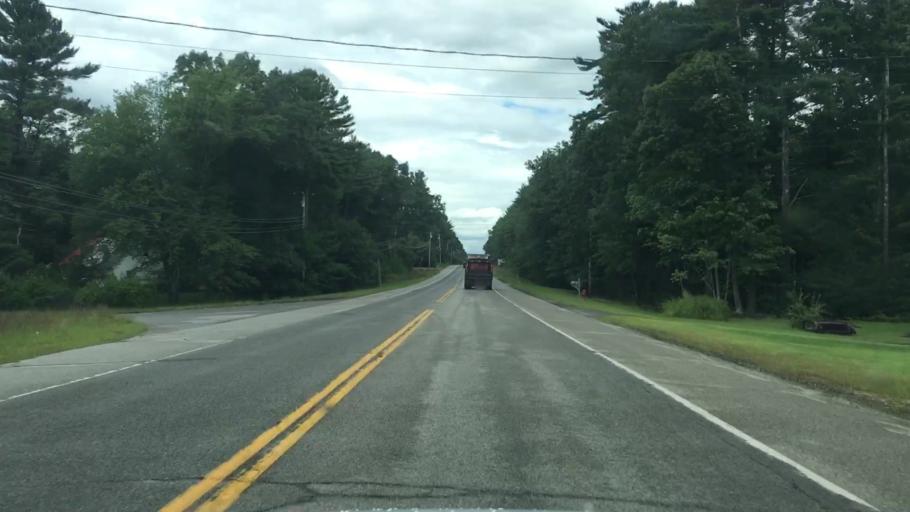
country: US
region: Maine
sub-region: York County
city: North Berwick
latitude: 43.3250
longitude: -70.7372
